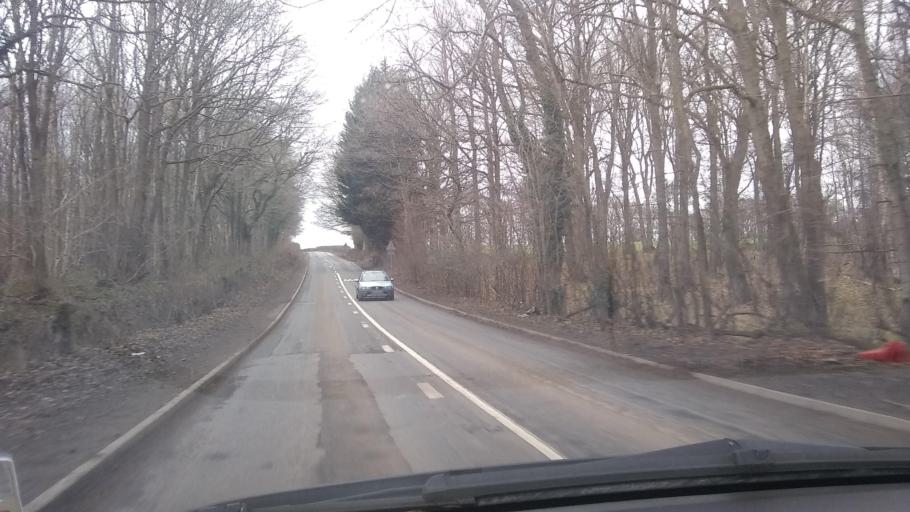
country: GB
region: England
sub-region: Shropshire
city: Cleobury Mortimer
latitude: 52.3771
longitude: -2.4394
